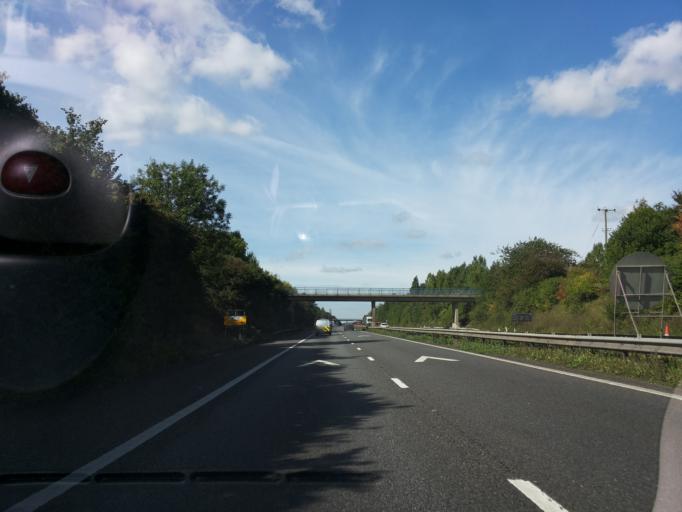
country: GB
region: England
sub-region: Kent
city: Sittingbourne
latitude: 51.3048
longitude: 0.7215
